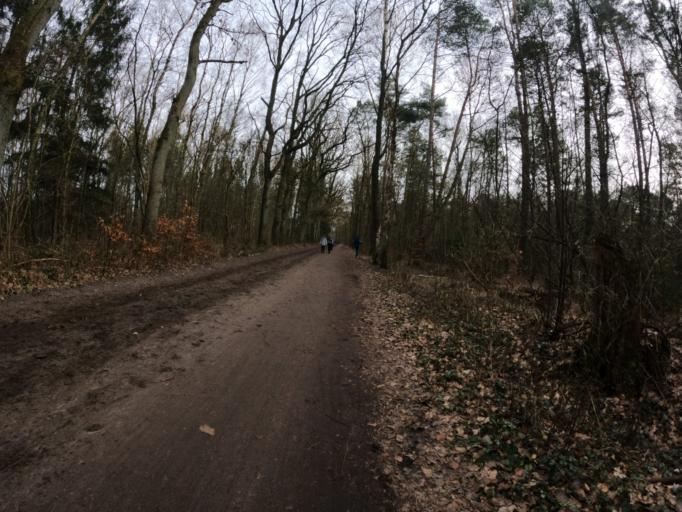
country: DE
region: Schleswig-Holstein
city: Appen
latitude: 53.6067
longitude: 9.7677
